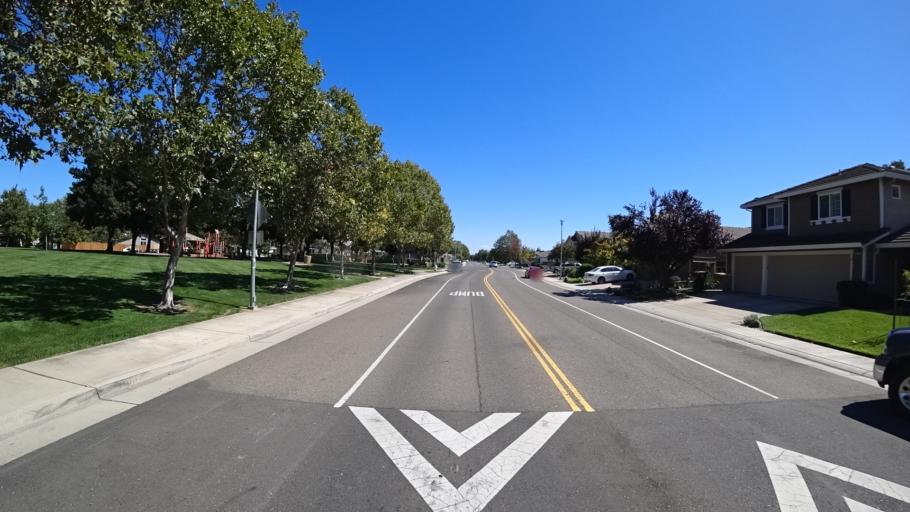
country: US
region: California
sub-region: Sacramento County
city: Elk Grove
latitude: 38.4023
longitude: -121.3491
